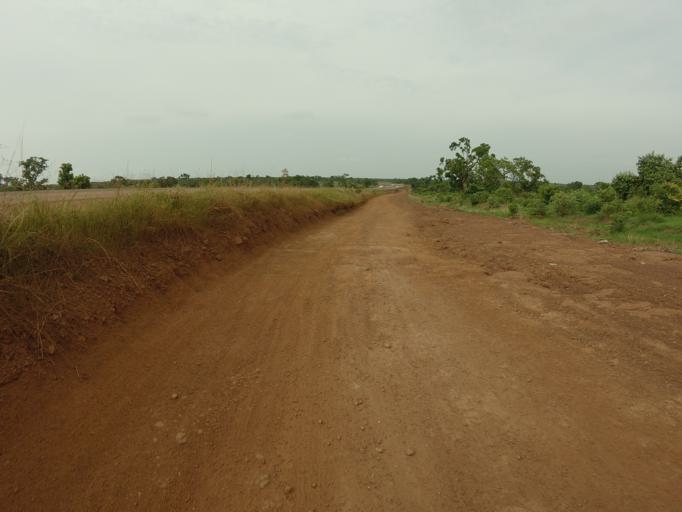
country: GH
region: Northern
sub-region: Yendi
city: Yendi
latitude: 9.7967
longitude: -0.1133
